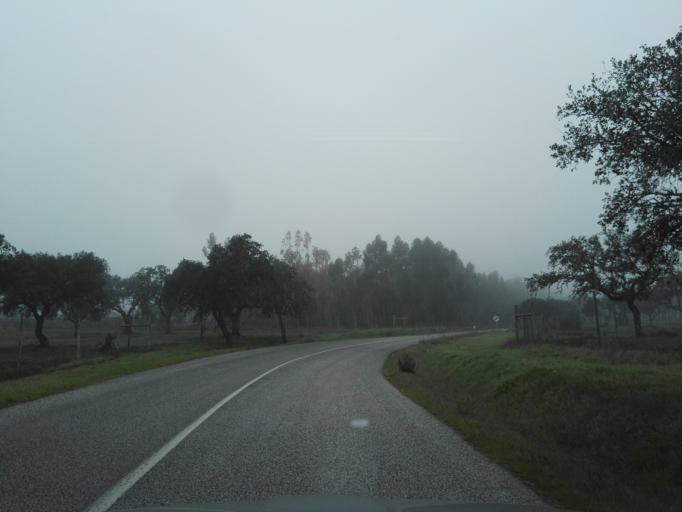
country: PT
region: Evora
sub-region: Montemor-O-Novo
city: Montemor-o-Novo
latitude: 38.7783
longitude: -8.2122
